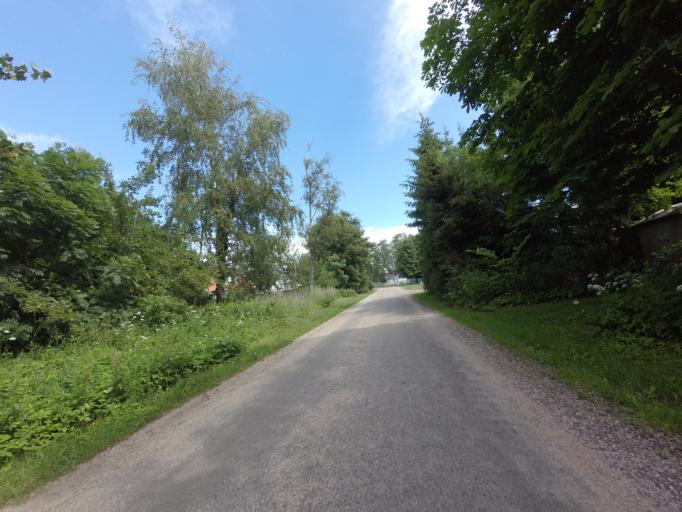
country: SE
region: Skane
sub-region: Skurups Kommun
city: Skivarp
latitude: 55.3822
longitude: 13.4749
